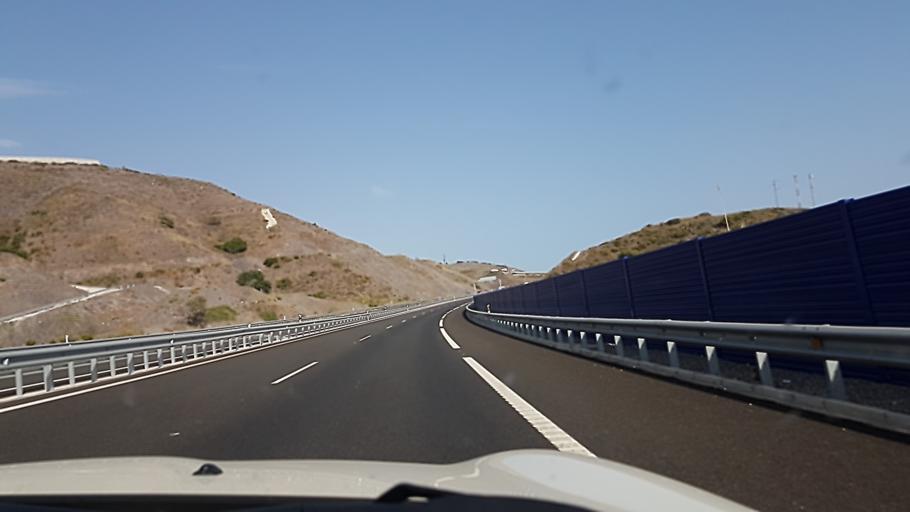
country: ES
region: Andalusia
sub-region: Provincia de Granada
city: Albunol
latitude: 36.7573
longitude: -3.2380
